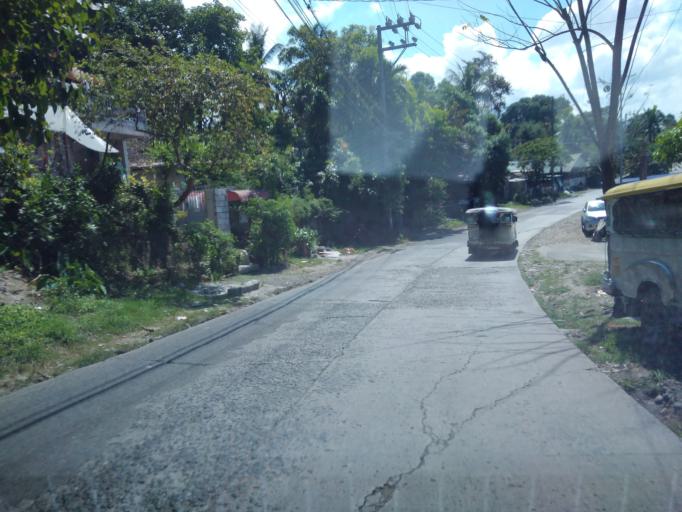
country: PH
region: Central Luzon
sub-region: Province of Bulacan
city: Bitungol
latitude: 14.8646
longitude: 121.0700
